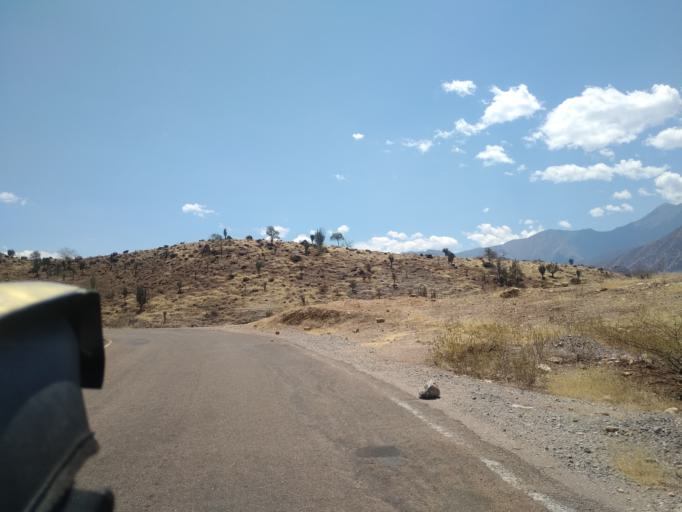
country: PE
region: Amazonas
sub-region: Provincia de Chachapoyas
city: Balsas
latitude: -6.8543
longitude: -78.0297
